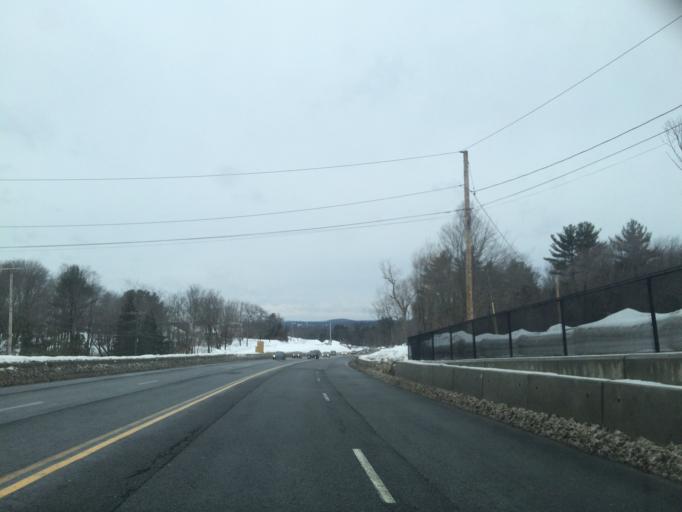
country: US
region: Massachusetts
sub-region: Middlesex County
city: Lincoln
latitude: 42.4471
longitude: -71.3134
